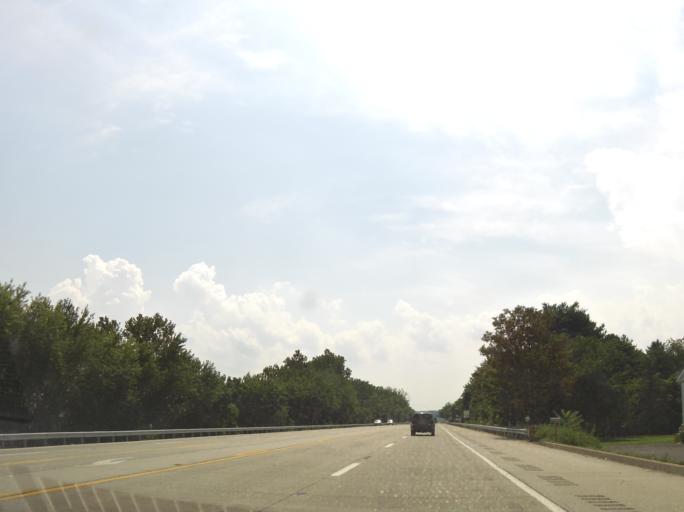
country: US
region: Pennsylvania
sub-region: Dauphin County
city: Matamoras
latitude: 40.4528
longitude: -76.9709
